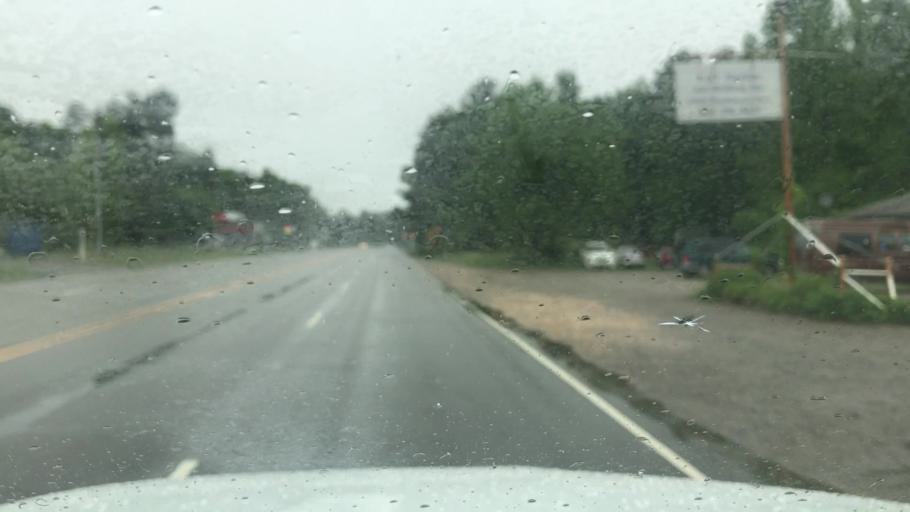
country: US
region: Virginia
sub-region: Hanover County
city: Ashland
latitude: 37.8162
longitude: -77.4740
